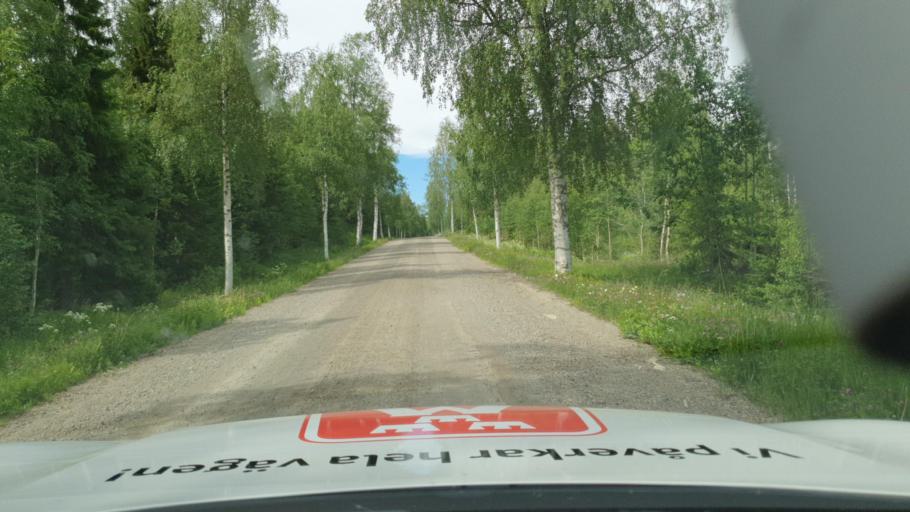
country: SE
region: Vaesterbotten
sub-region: Skelleftea Kommun
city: Burtraesk
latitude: 64.4713
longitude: 20.4532
